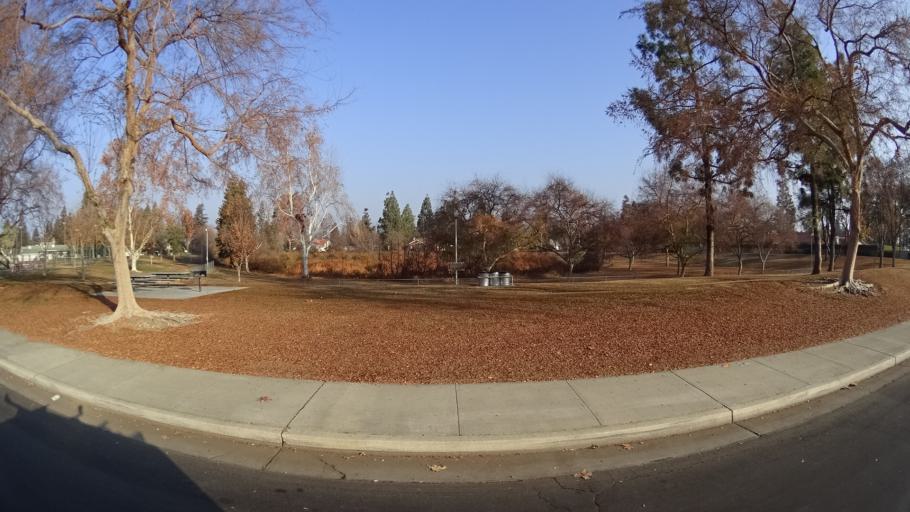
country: US
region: California
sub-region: Kern County
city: Greenacres
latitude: 35.3314
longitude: -119.1030
